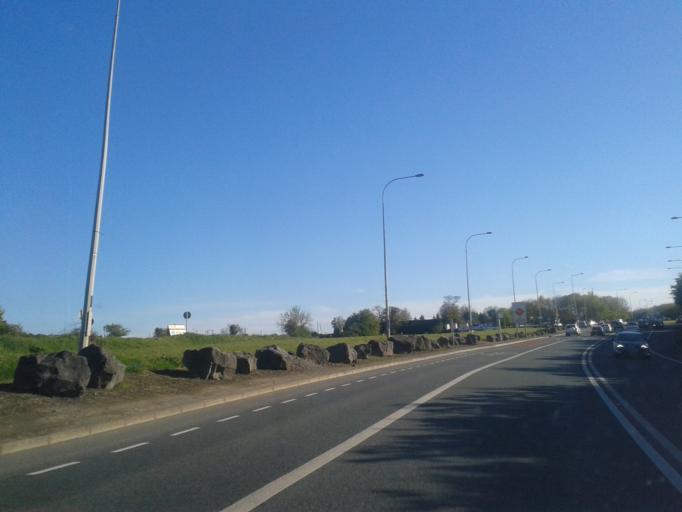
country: IE
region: Leinster
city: Kinsealy-Drinan
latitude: 53.4358
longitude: -6.2276
